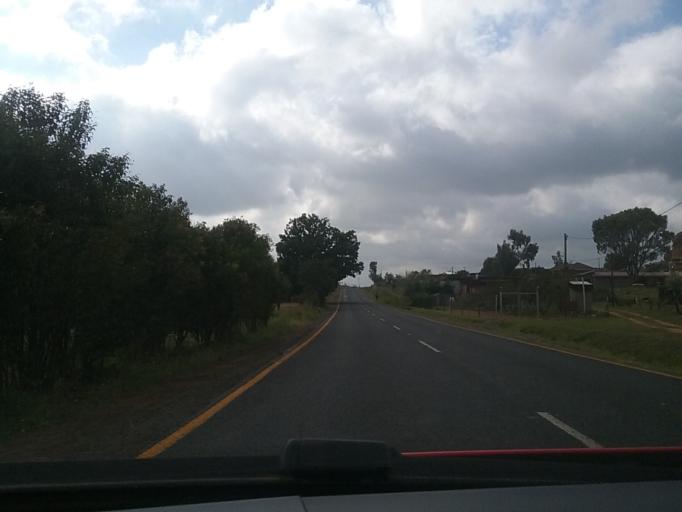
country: LS
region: Berea
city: Teyateyaneng
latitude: -29.1584
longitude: 27.7564
